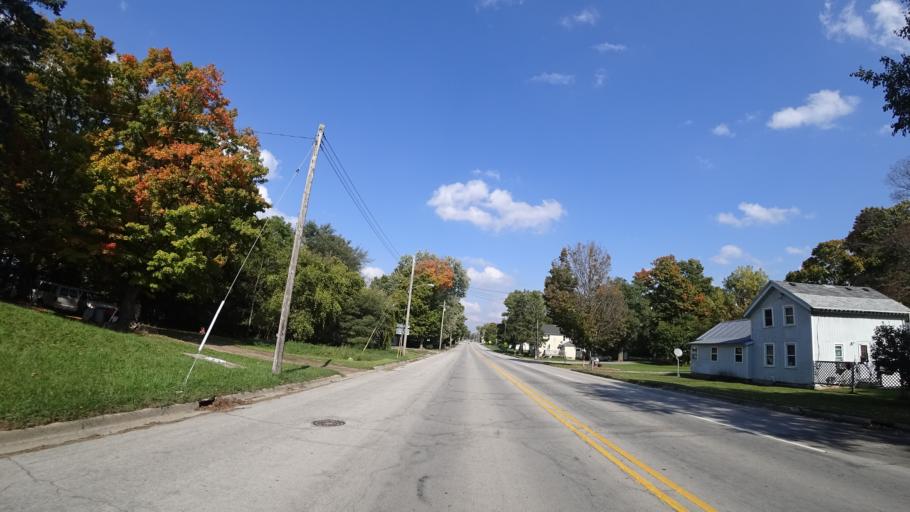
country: US
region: Michigan
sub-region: Saint Joseph County
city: Colon
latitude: 42.0209
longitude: -85.3542
